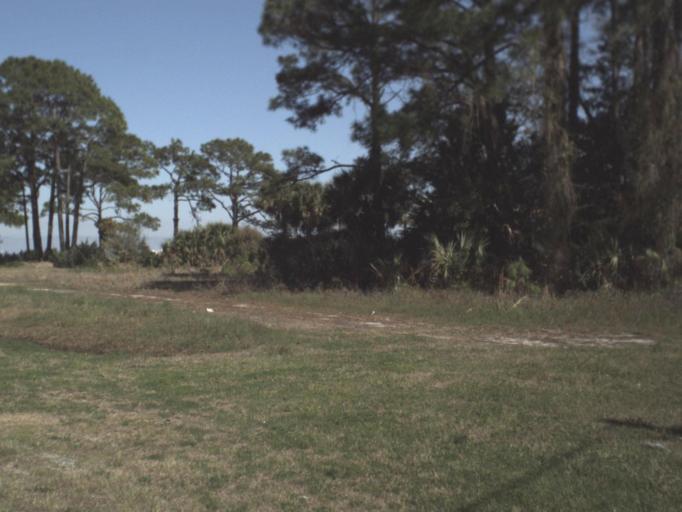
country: US
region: Florida
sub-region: Franklin County
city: Carrabelle
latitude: 29.8748
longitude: -84.6058
